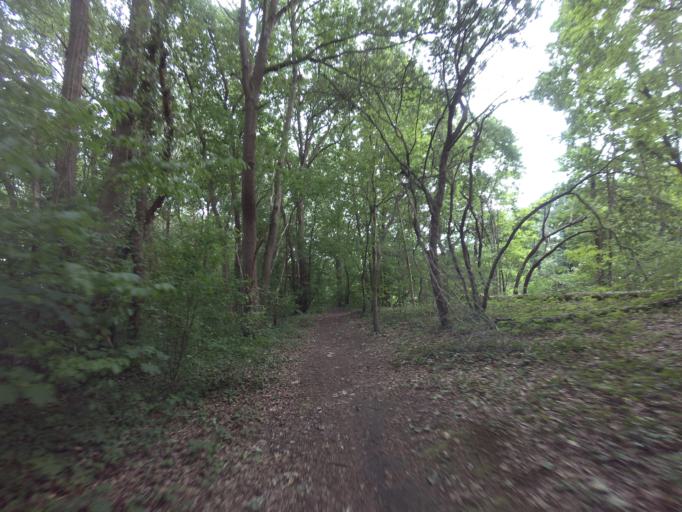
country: BE
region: Flanders
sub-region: Provincie Antwerpen
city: Mechelen
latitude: 51.0625
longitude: 4.4651
